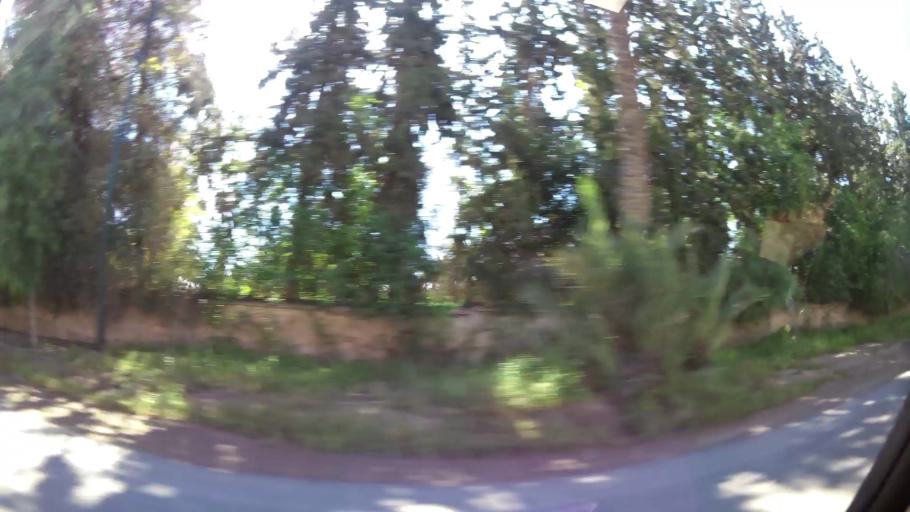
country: MA
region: Marrakech-Tensift-Al Haouz
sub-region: Marrakech
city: Marrakesh
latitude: 31.6555
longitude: -7.9735
